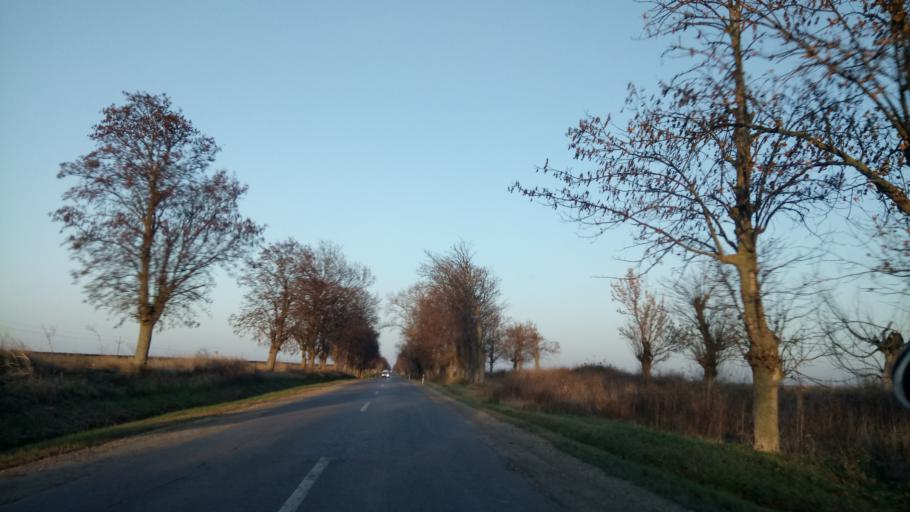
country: RS
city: Novi Karlovci
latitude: 45.1018
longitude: 20.2075
